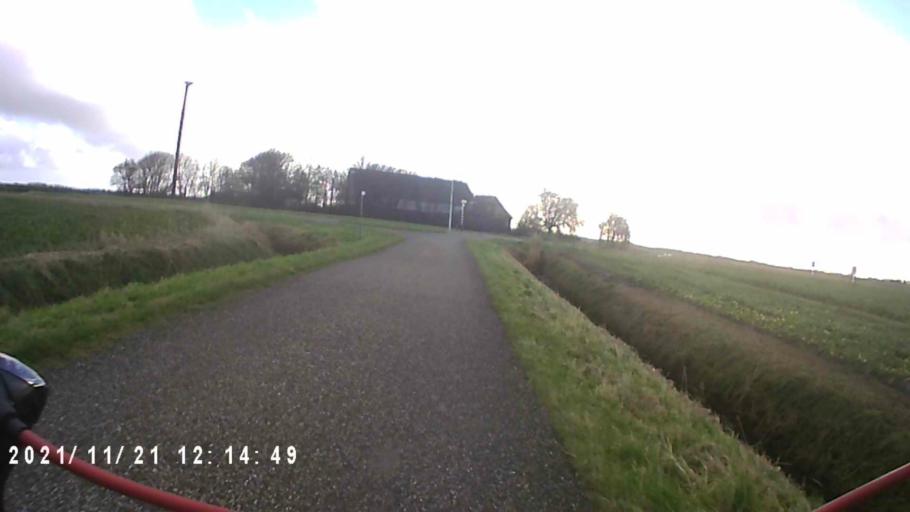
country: NL
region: Friesland
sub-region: Gemeente Dongeradeel
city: Ternaard
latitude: 53.3860
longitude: 6.0073
